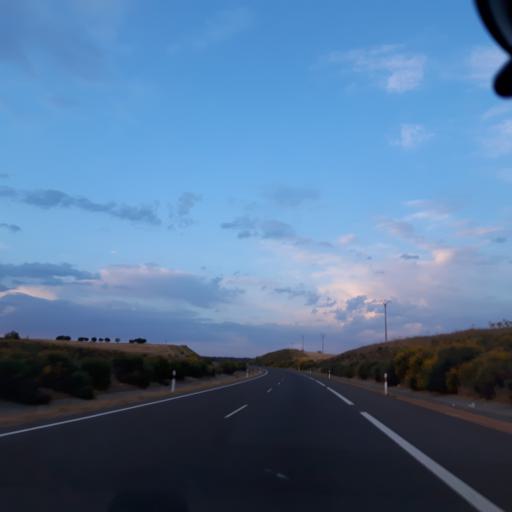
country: ES
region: Castille and Leon
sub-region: Provincia de Salamanca
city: Mozarbez
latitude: 40.8475
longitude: -5.6413
